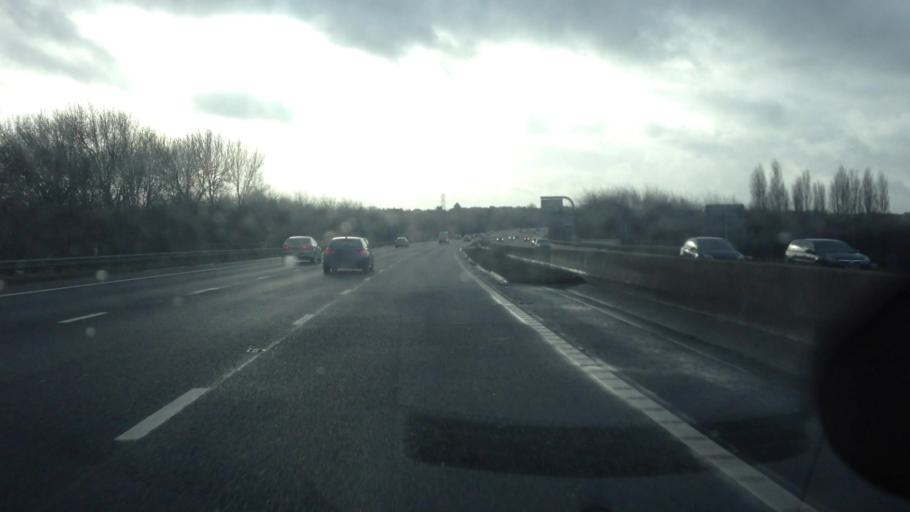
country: GB
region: England
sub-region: City and Borough of Wakefield
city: Crigglestone
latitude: 53.6524
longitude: -1.5280
